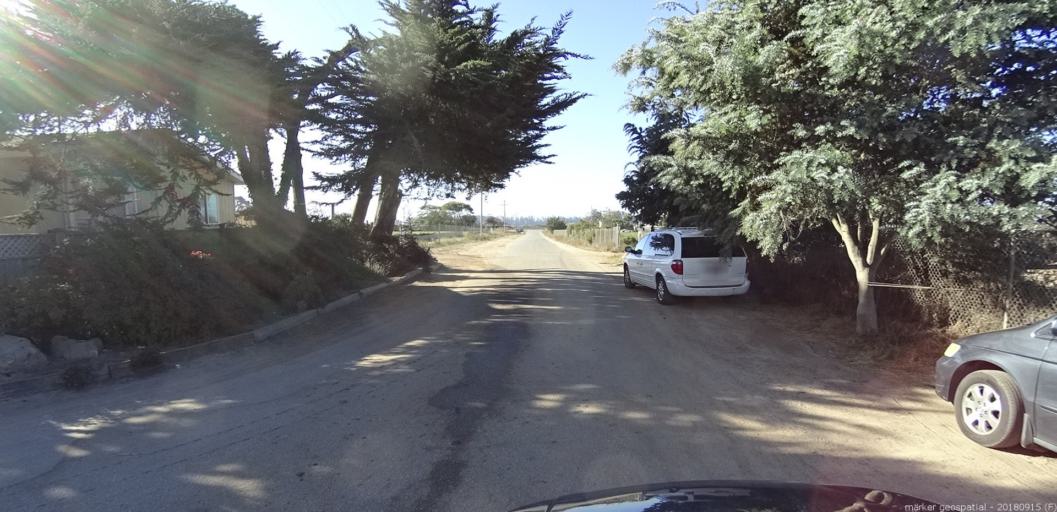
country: US
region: California
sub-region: Monterey County
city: Elkhorn
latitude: 36.8335
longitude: -121.7745
